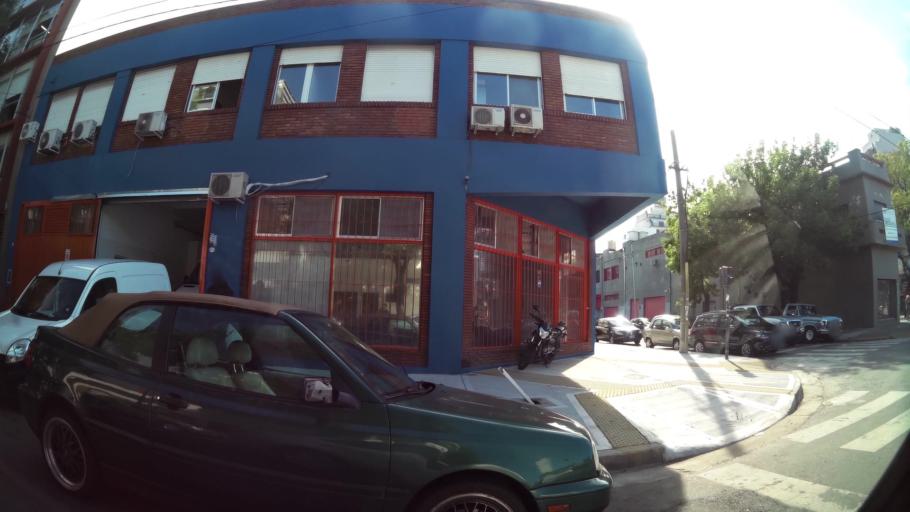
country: AR
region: Buenos Aires
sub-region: Partido de General San Martin
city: General San Martin
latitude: -34.5548
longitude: -58.4926
